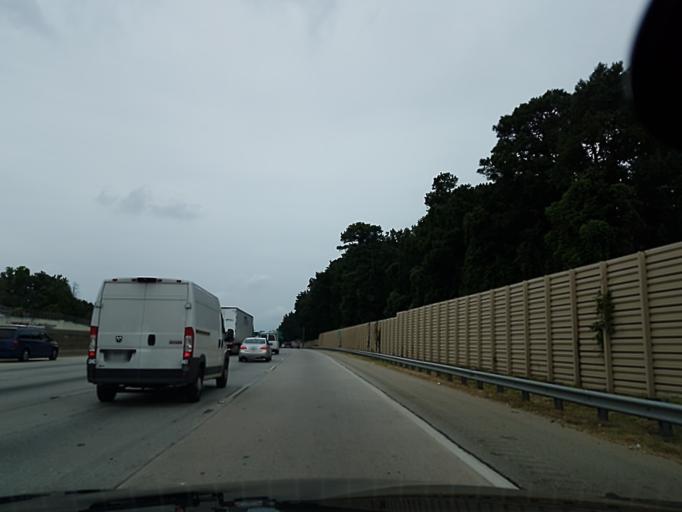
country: US
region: Georgia
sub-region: DeKalb County
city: Clarkston
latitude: 33.8247
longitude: -84.2529
